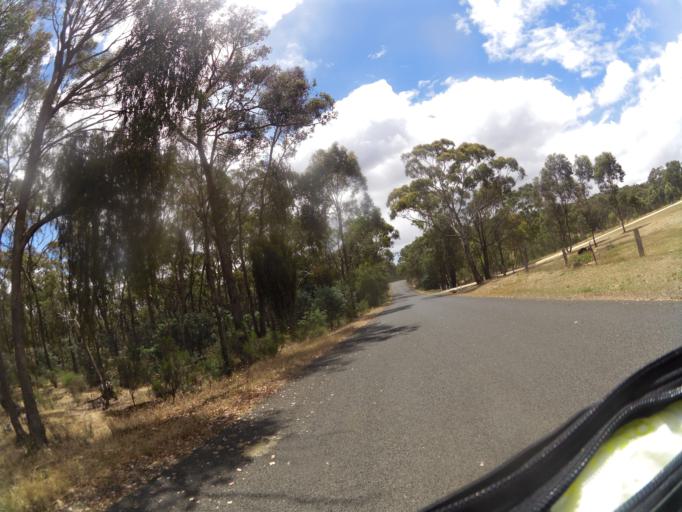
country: AU
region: Victoria
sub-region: Mount Alexander
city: Castlemaine
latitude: -37.0235
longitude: 144.2419
